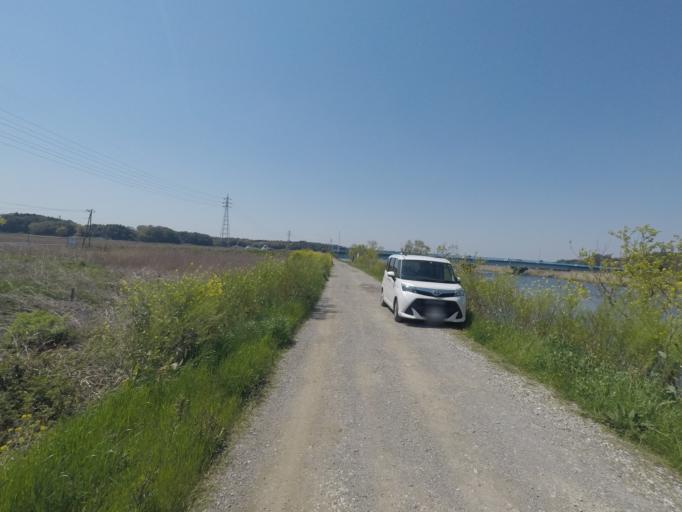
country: JP
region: Ibaraki
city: Ushiku
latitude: 35.9531
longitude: 140.1041
